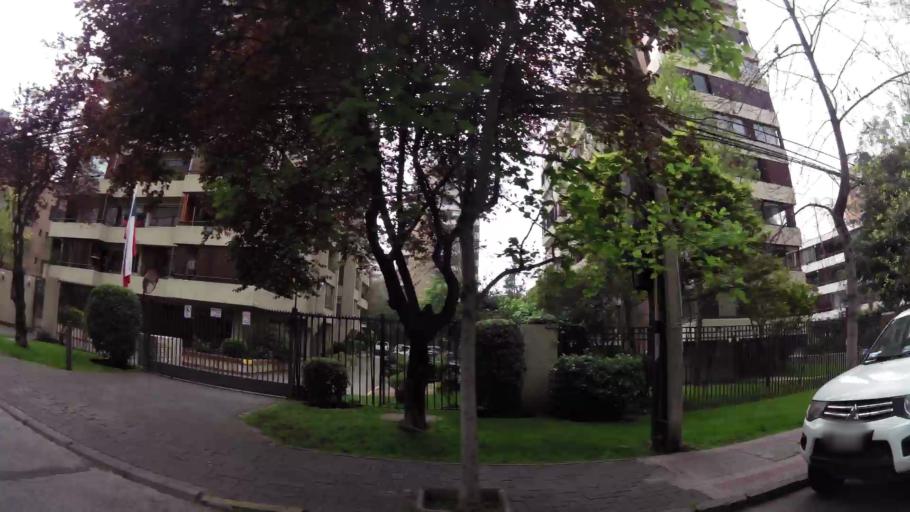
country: CL
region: Santiago Metropolitan
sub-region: Provincia de Santiago
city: Villa Presidente Frei, Nunoa, Santiago, Chile
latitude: -33.4320
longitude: -70.5980
